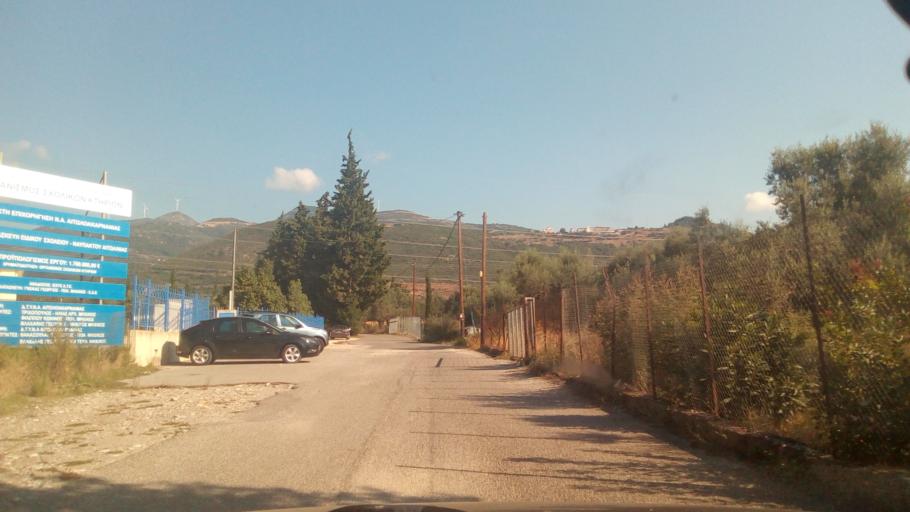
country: GR
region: West Greece
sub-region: Nomos Aitolias kai Akarnanias
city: Nafpaktos
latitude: 38.4024
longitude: 21.8463
